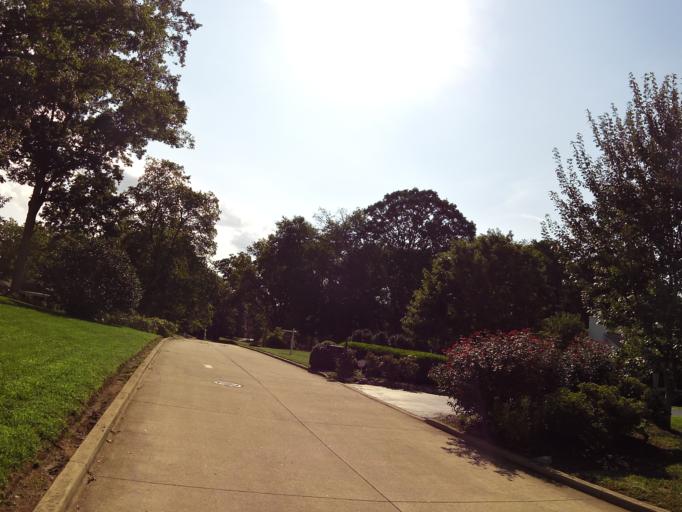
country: US
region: Tennessee
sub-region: Knox County
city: Knoxville
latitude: 35.9361
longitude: -83.9620
